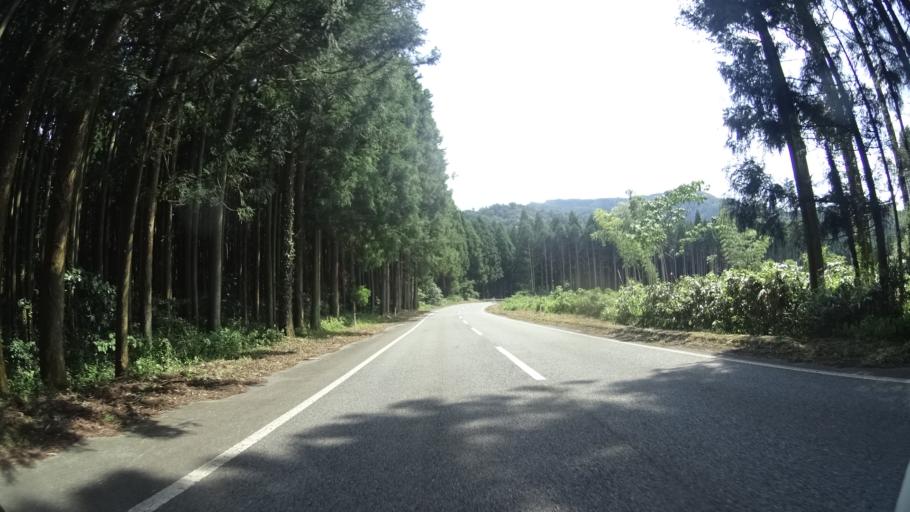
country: JP
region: Yamaguchi
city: Hagi
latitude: 34.4952
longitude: 131.5526
